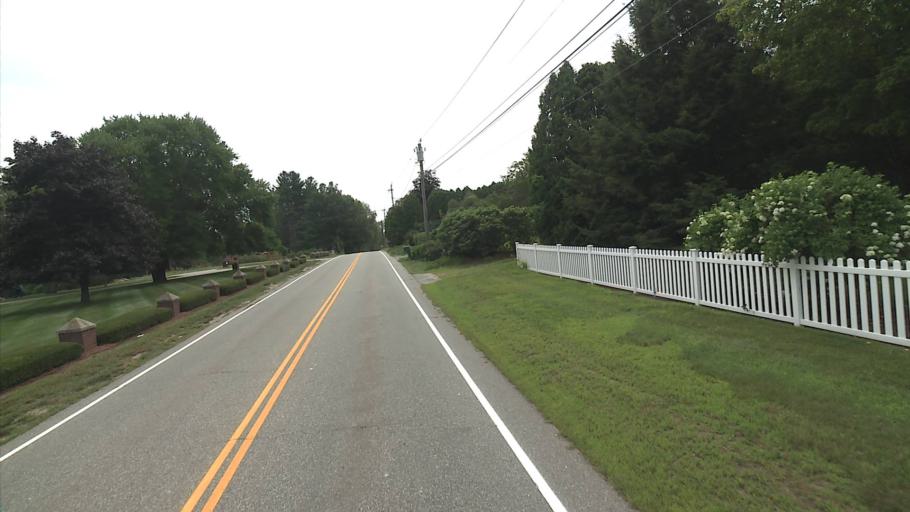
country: US
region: Connecticut
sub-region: Windham County
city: Wauregan
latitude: 41.7573
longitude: -71.9247
